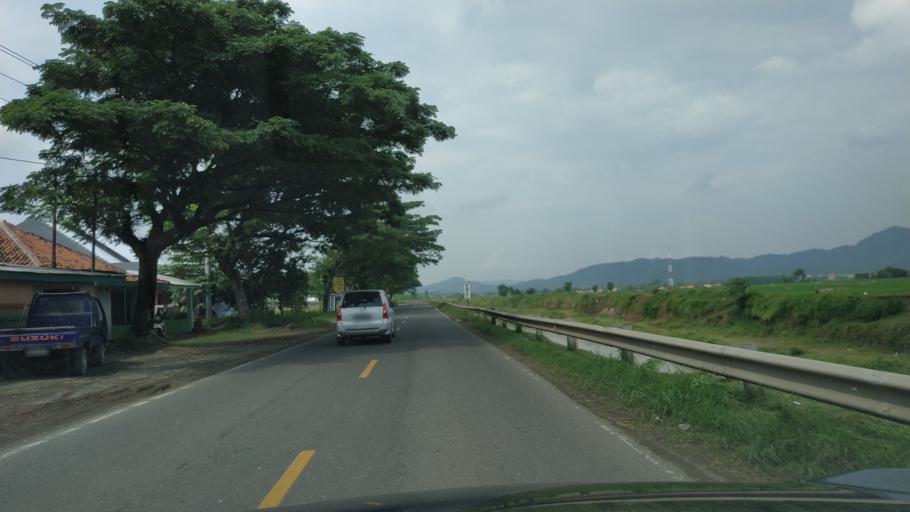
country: ID
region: Central Java
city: Margasari
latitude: -7.0796
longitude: 108.9825
